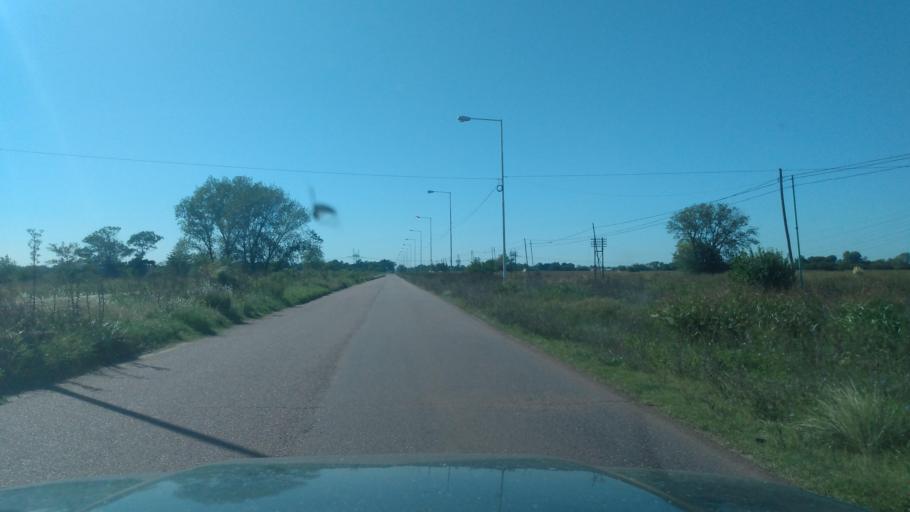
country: AR
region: Buenos Aires
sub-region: Partido de Lujan
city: Lujan
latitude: -34.5895
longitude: -59.0346
